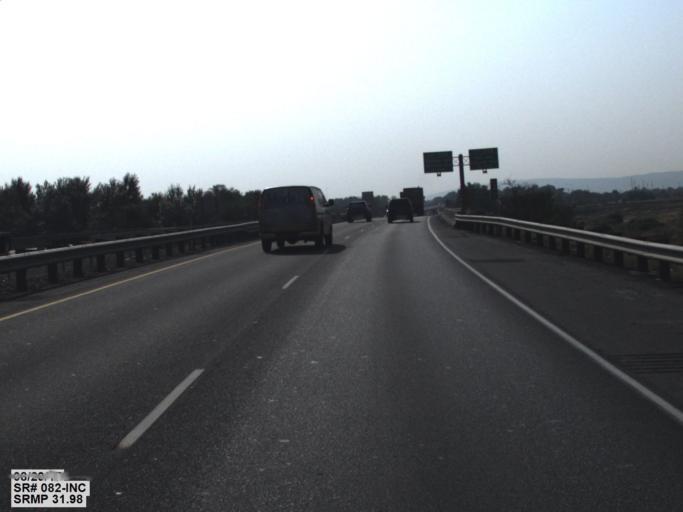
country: US
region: Washington
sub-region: Yakima County
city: Yakima
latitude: 46.6213
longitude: -120.4977
